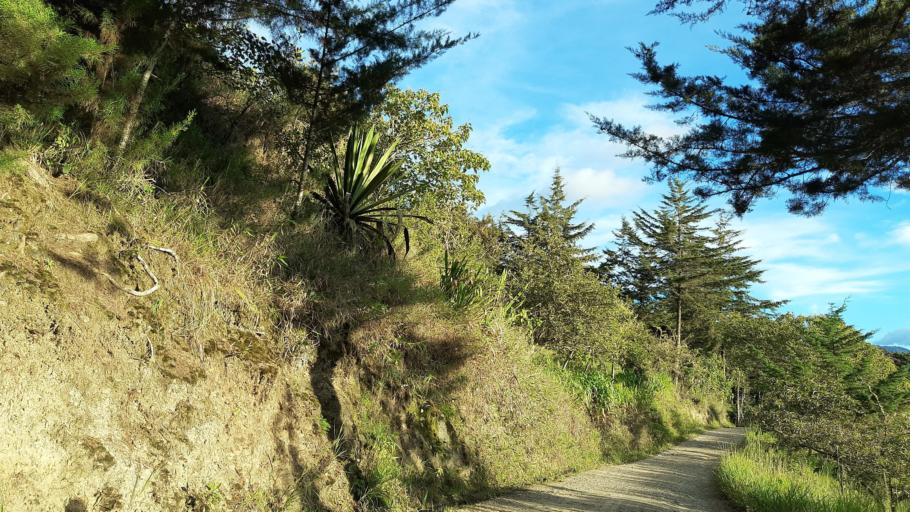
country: CO
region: Boyaca
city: Garagoa
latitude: 5.0639
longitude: -73.3771
